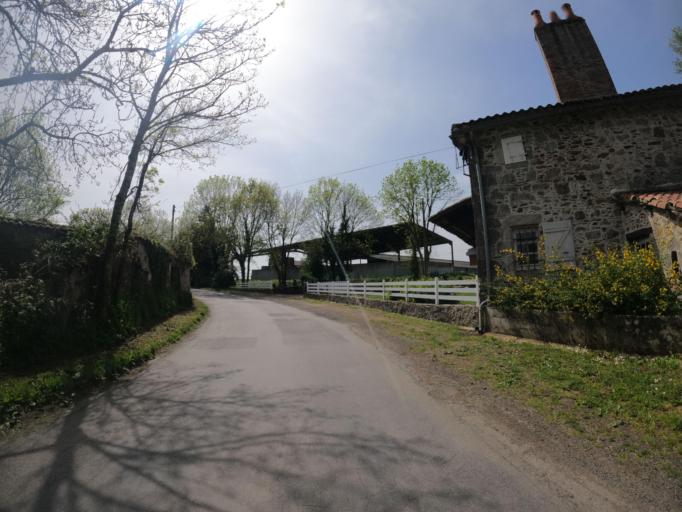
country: FR
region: Poitou-Charentes
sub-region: Departement des Deux-Sevres
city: La Chapelle-Saint-Laurent
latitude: 46.7122
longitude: -0.5102
